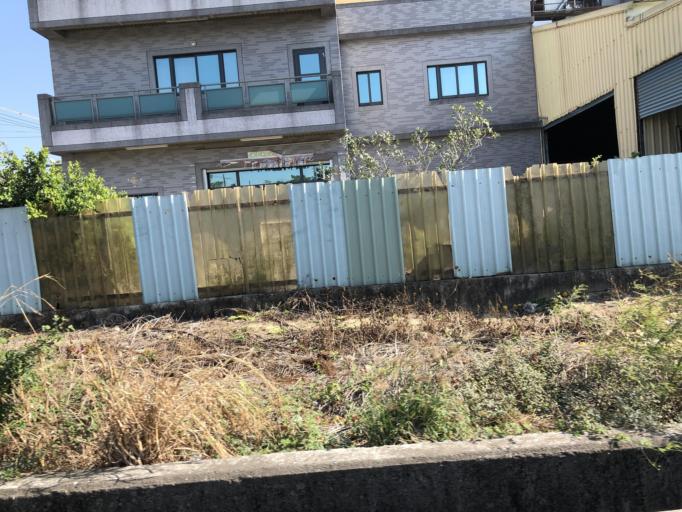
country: TW
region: Taiwan
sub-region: Tainan
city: Tainan
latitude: 23.0382
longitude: 120.3215
